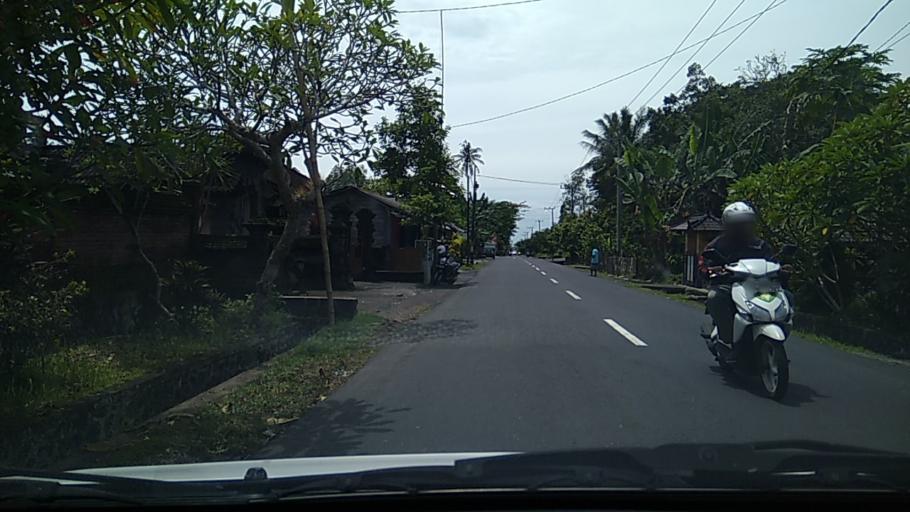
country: ID
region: Bali
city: Wanasari Baleran
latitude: -8.4790
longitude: 115.1360
